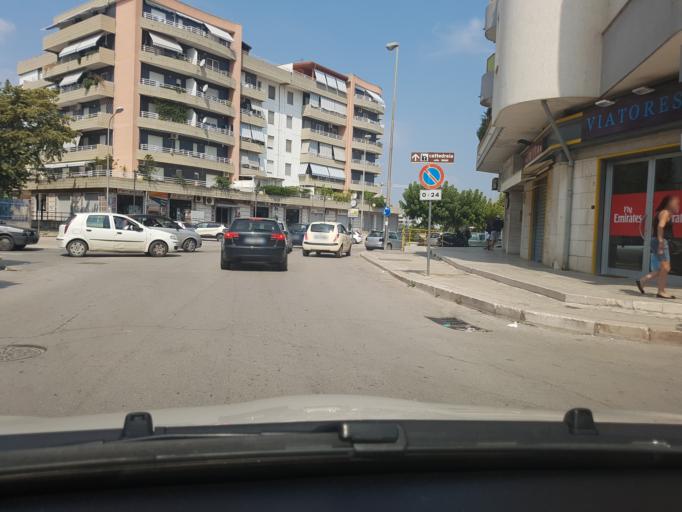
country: IT
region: Apulia
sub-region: Provincia di Foggia
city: Cerignola
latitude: 41.2651
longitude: 15.9090
